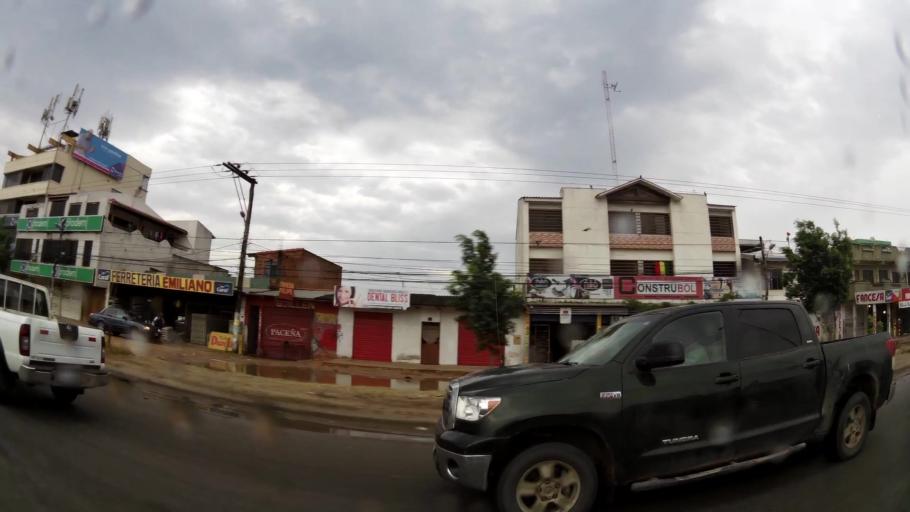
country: BO
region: Santa Cruz
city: Santa Cruz de la Sierra
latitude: -17.7688
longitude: -63.1188
